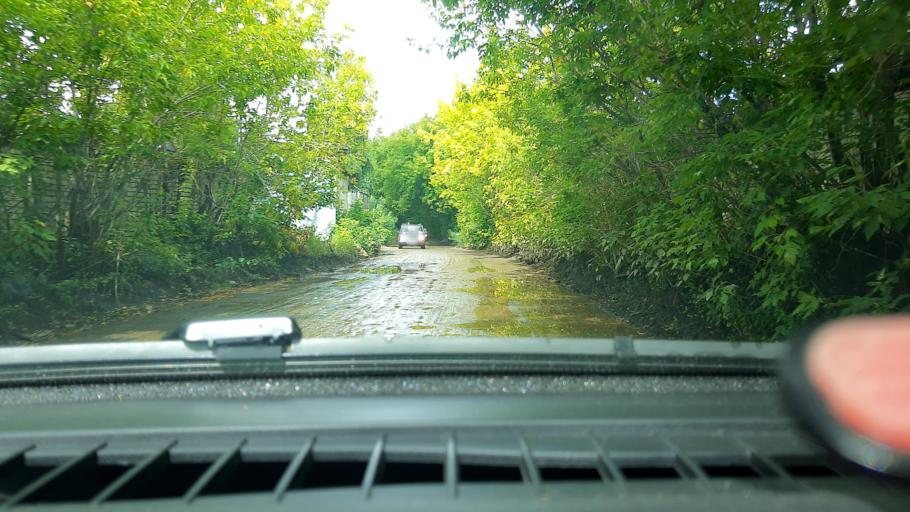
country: RU
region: Nizjnij Novgorod
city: Gorbatovka
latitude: 56.2551
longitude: 43.8320
